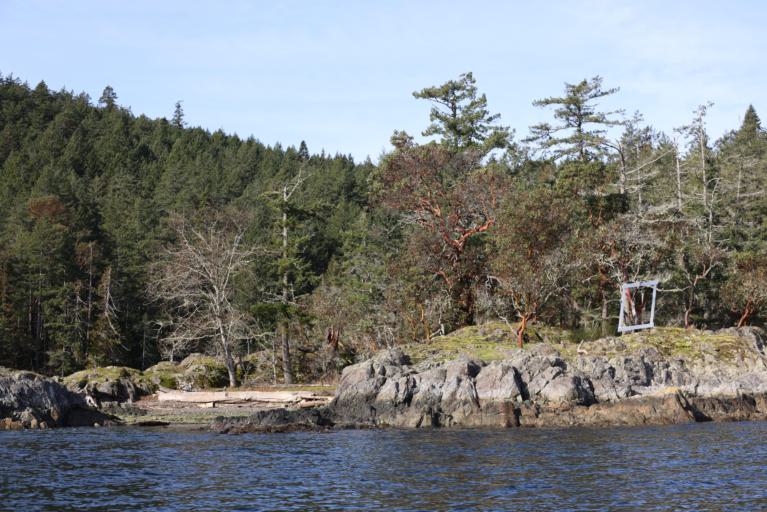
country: CA
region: British Columbia
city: Duncan
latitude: 48.7694
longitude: -123.5770
